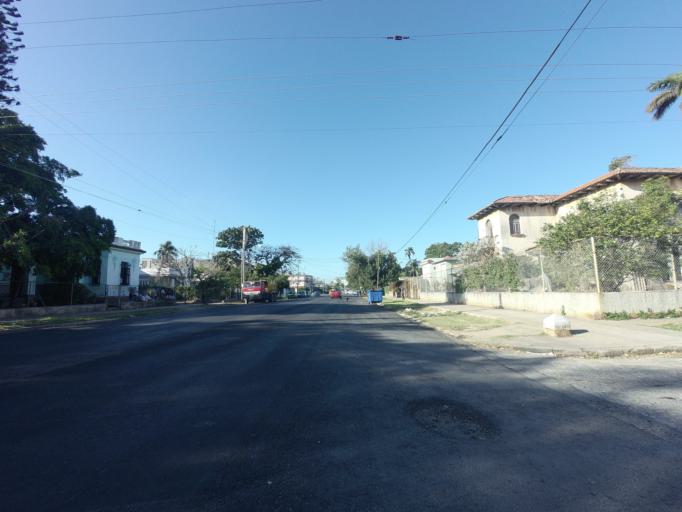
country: CU
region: La Habana
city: Cerro
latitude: 23.1006
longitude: -82.4365
